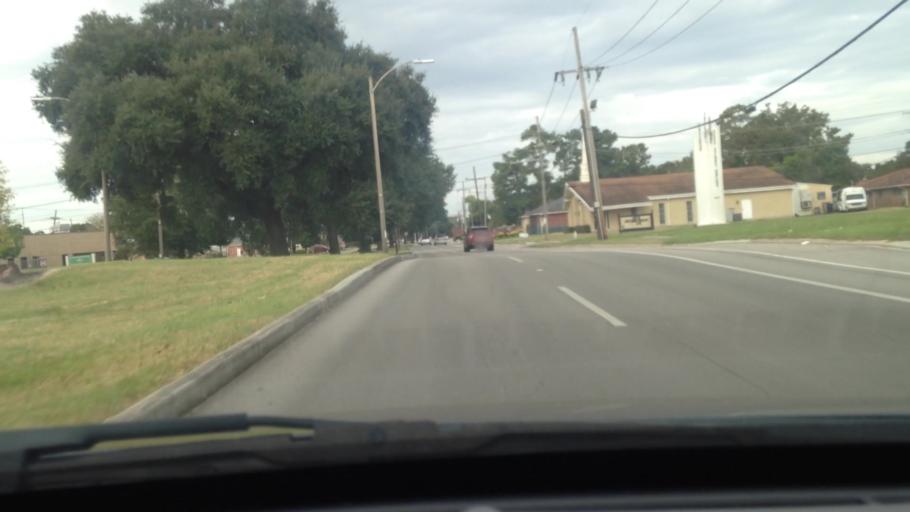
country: US
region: Louisiana
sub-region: Jefferson Parish
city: Terrytown
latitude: 29.9246
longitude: -90.0143
